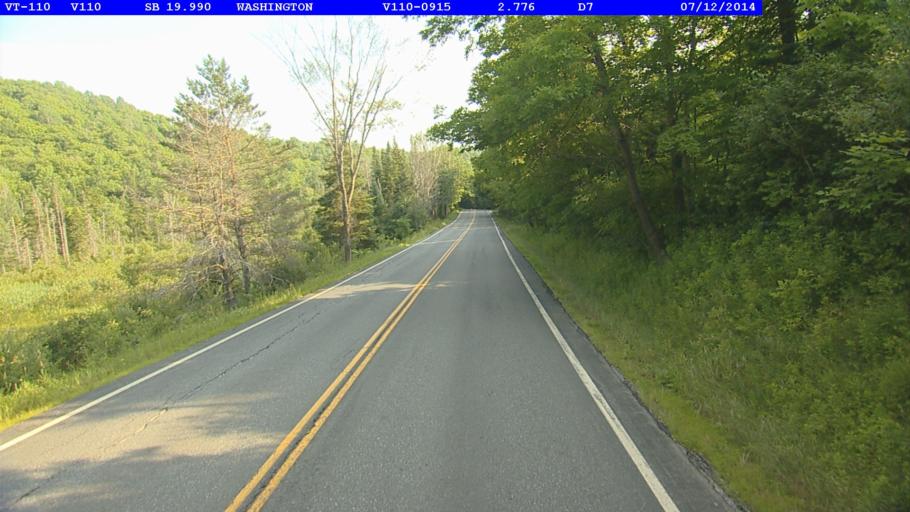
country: US
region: Vermont
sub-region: Orange County
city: Chelsea
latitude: 44.0748
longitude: -72.4617
